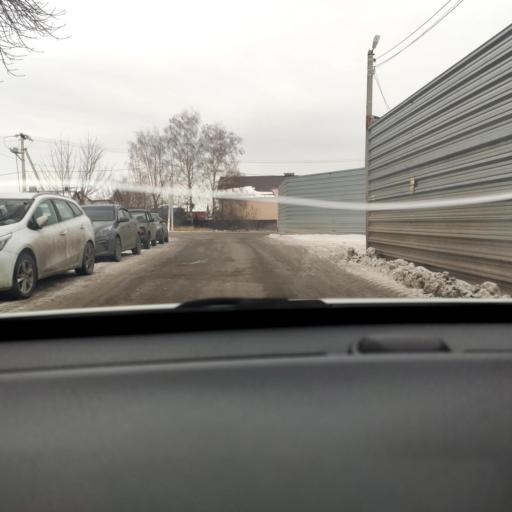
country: RU
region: Voronezj
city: Novaya Usman'
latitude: 51.6683
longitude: 39.3348
